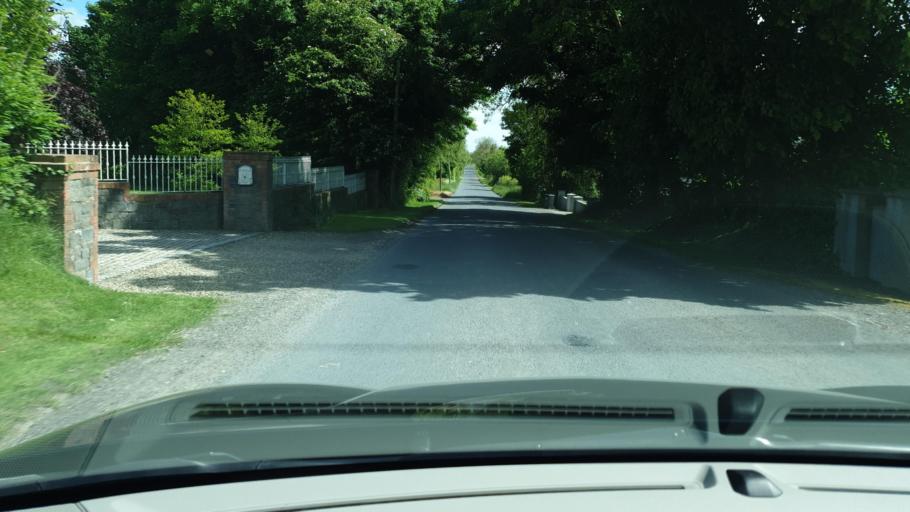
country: IE
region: Leinster
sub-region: An Mhi
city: Slane
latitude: 53.7594
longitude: -6.6083
